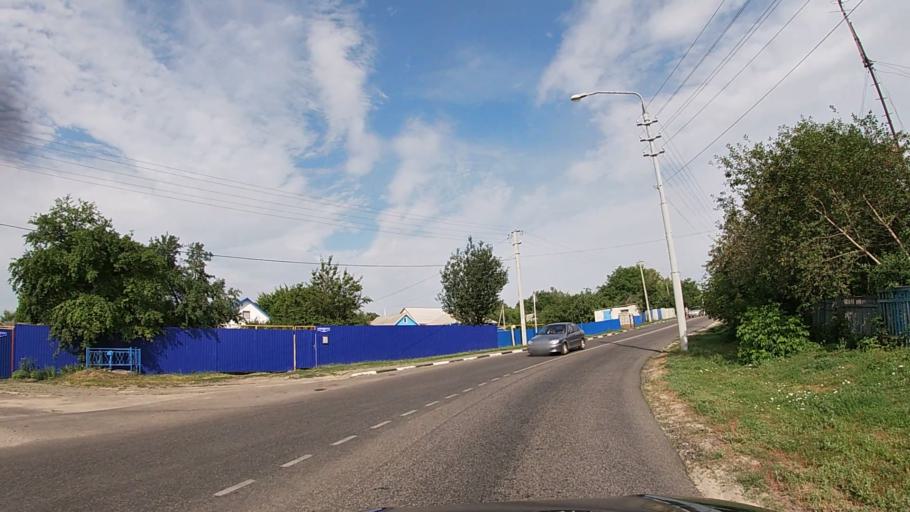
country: RU
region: Belgorod
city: Krasnaya Yaruga
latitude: 50.7996
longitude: 35.6631
